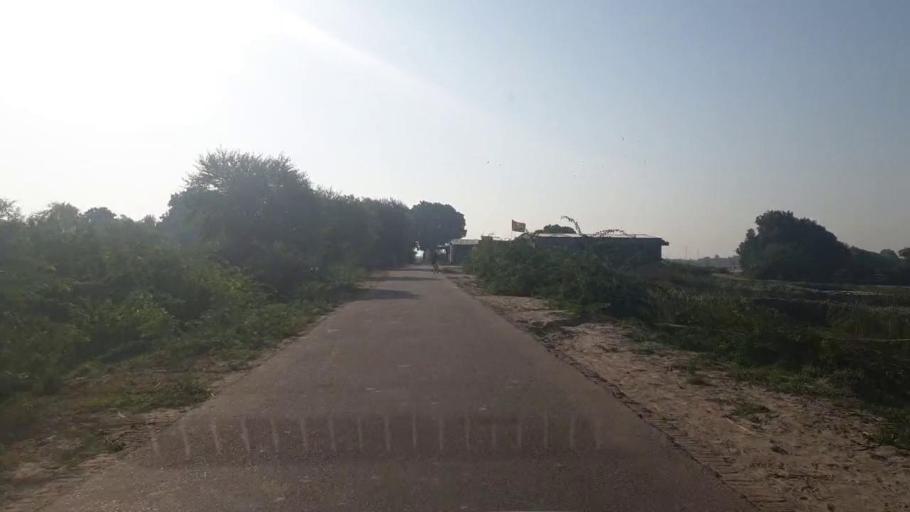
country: PK
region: Sindh
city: Tando Bago
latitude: 24.7213
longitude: 68.9401
